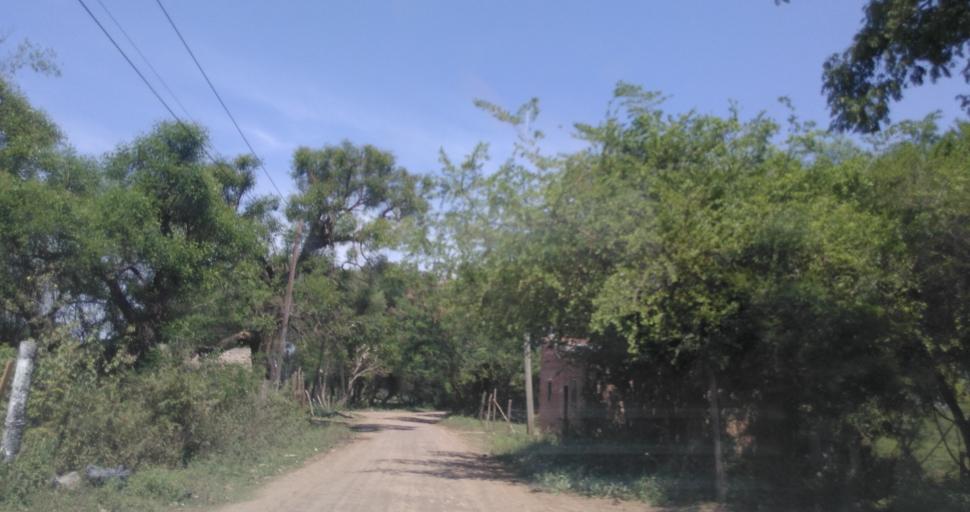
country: AR
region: Chaco
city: Fontana
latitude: -27.4158
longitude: -59.0111
